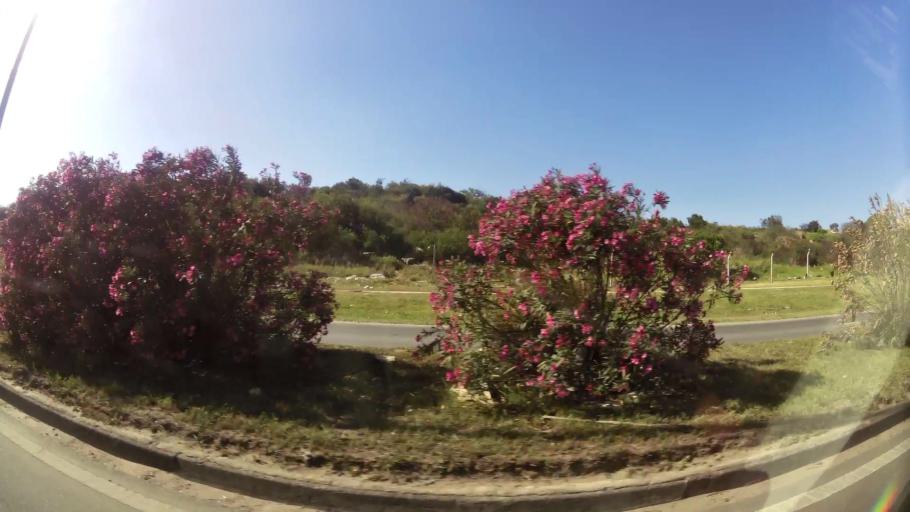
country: AR
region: Cordoba
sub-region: Departamento de Capital
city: Cordoba
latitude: -31.3983
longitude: -64.1349
